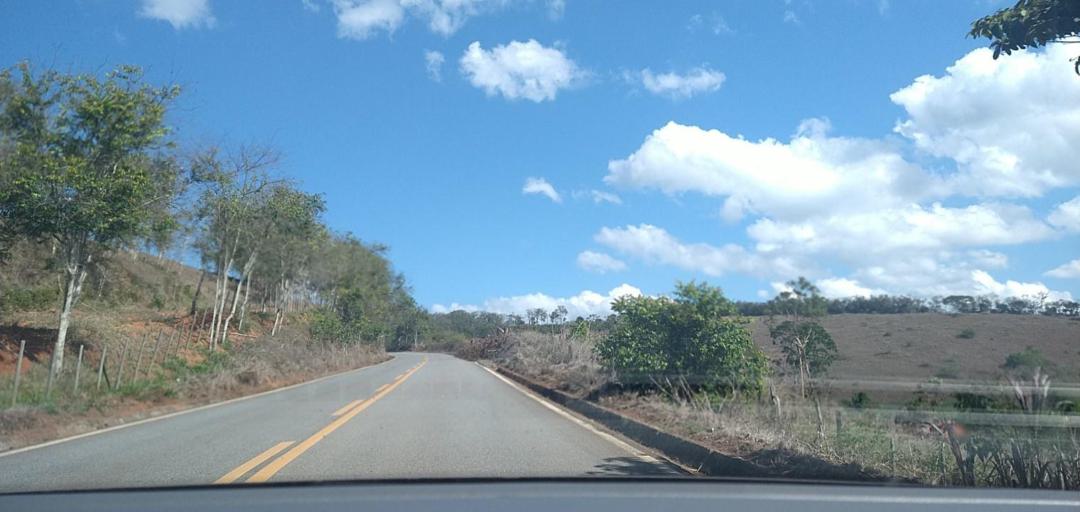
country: BR
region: Minas Gerais
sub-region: Alvinopolis
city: Alvinopolis
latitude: -20.0335
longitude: -43.0461
